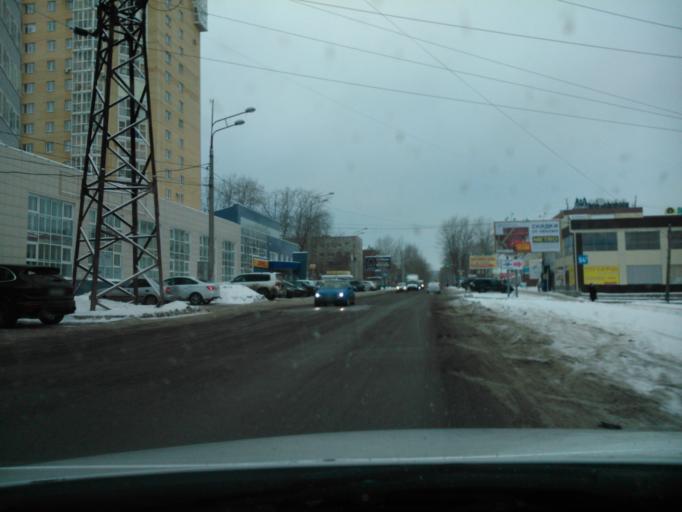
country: RU
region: Perm
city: Perm
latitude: 57.9875
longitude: 56.2089
